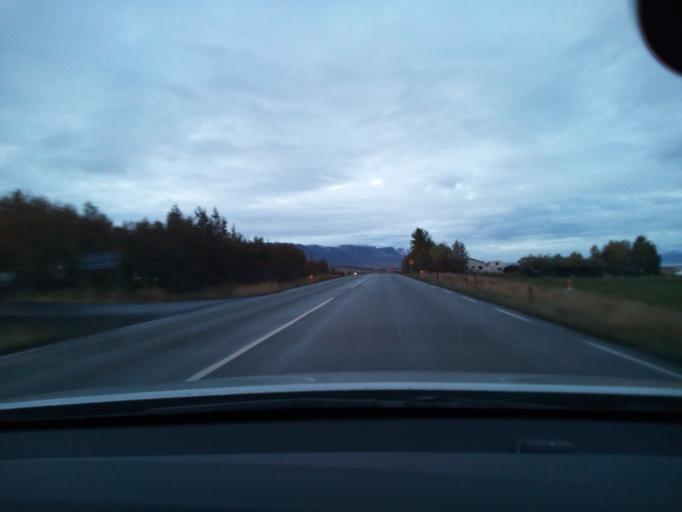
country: IS
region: Northeast
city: Akureyri
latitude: 65.7065
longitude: -18.1572
